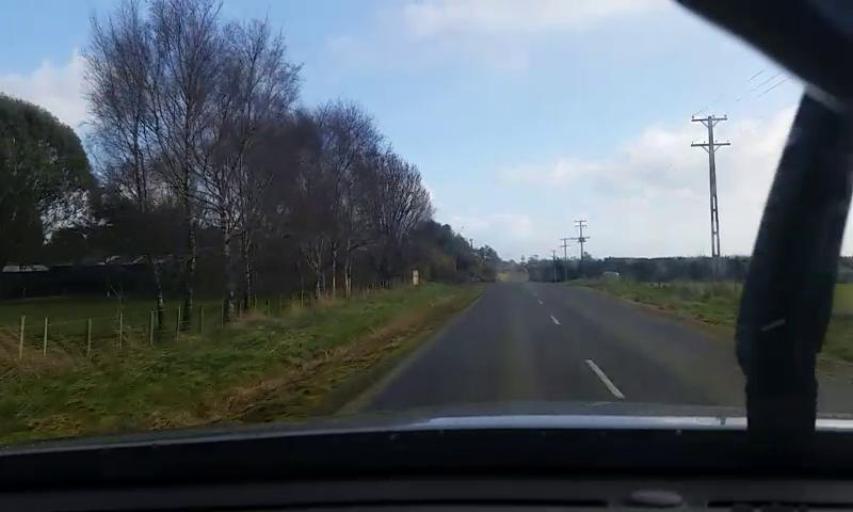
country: NZ
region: Southland
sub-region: Invercargill City
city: Invercargill
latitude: -46.3581
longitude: 168.3371
